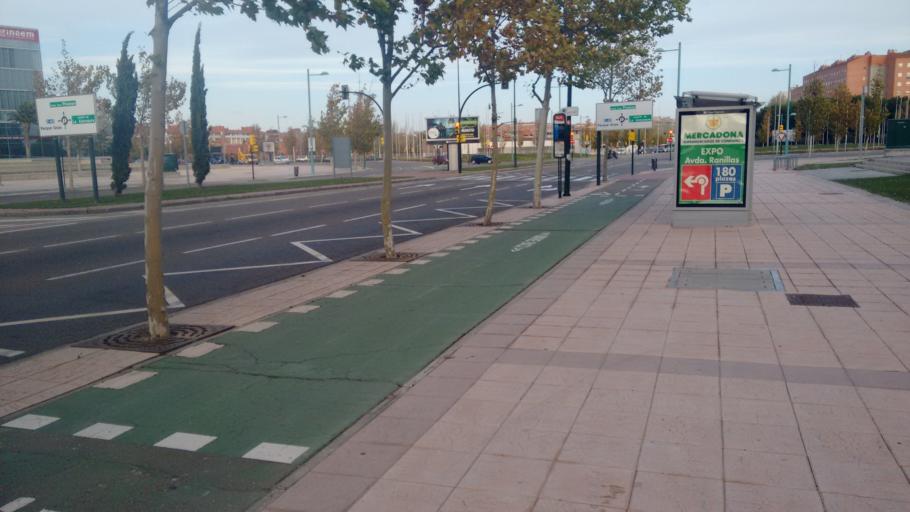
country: ES
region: Aragon
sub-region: Provincia de Zaragoza
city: Almozara
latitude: 41.6712
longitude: -0.8990
